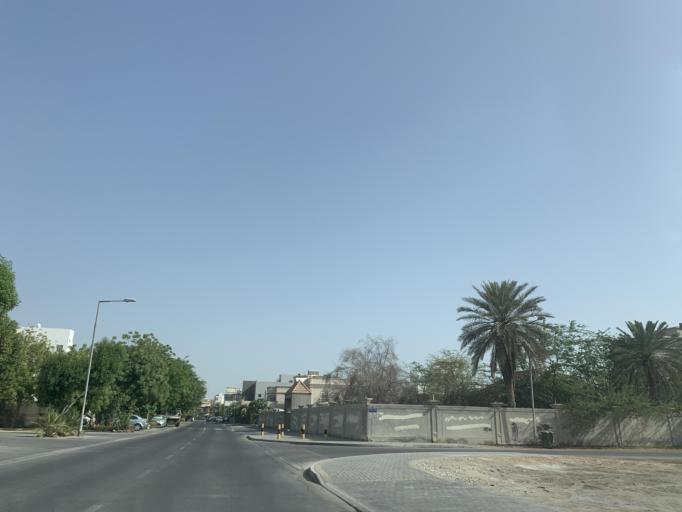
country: BH
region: Northern
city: Ar Rifa'
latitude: 26.1461
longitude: 50.5804
